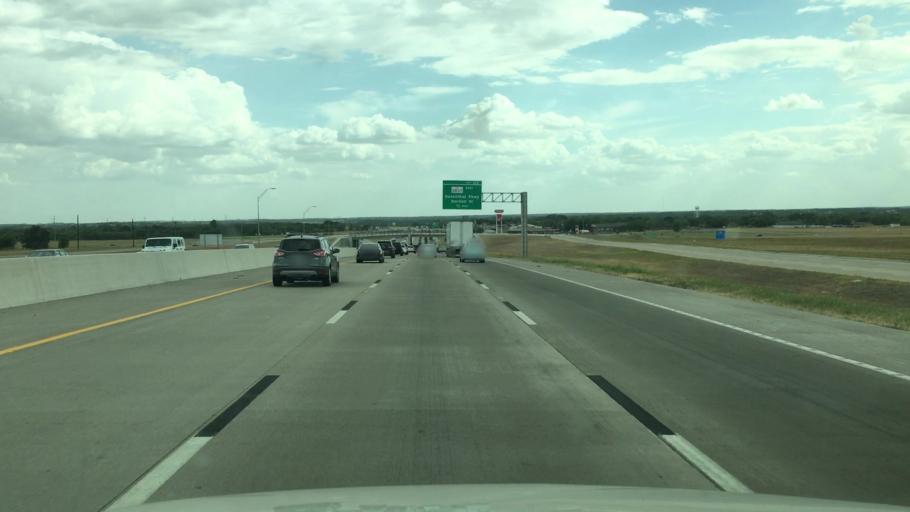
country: US
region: Texas
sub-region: McLennan County
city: Lorena
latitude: 31.3985
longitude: -97.2073
